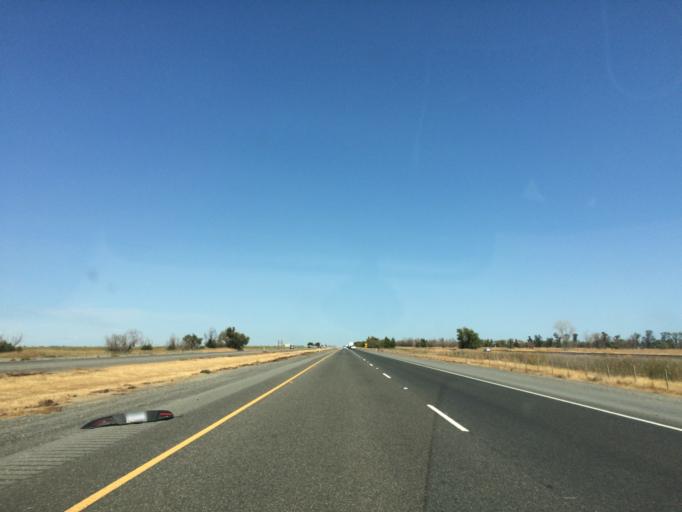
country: US
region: California
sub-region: Glenn County
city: Willows
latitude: 39.4216
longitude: -122.1932
